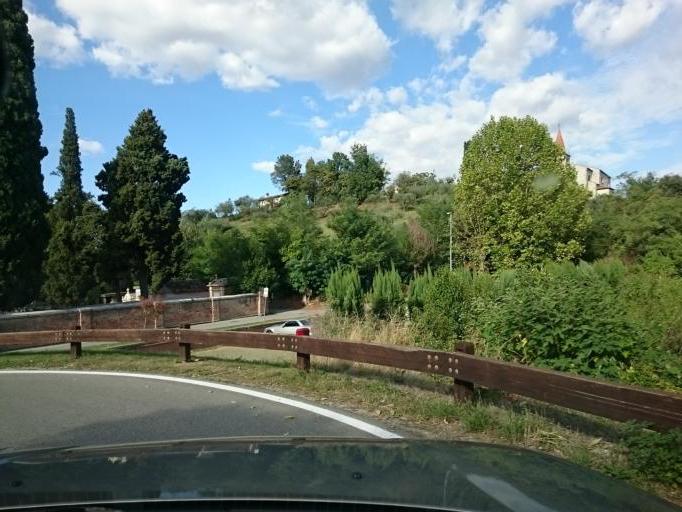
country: IT
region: Veneto
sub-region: Provincia di Padova
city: Torreglia
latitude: 45.3276
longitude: 11.7181
